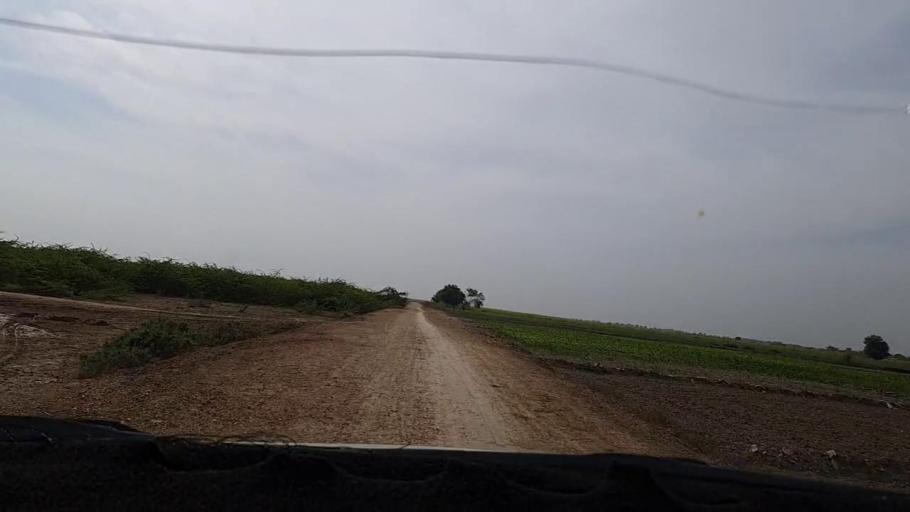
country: PK
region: Sindh
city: Pithoro
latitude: 25.5534
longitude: 69.3501
